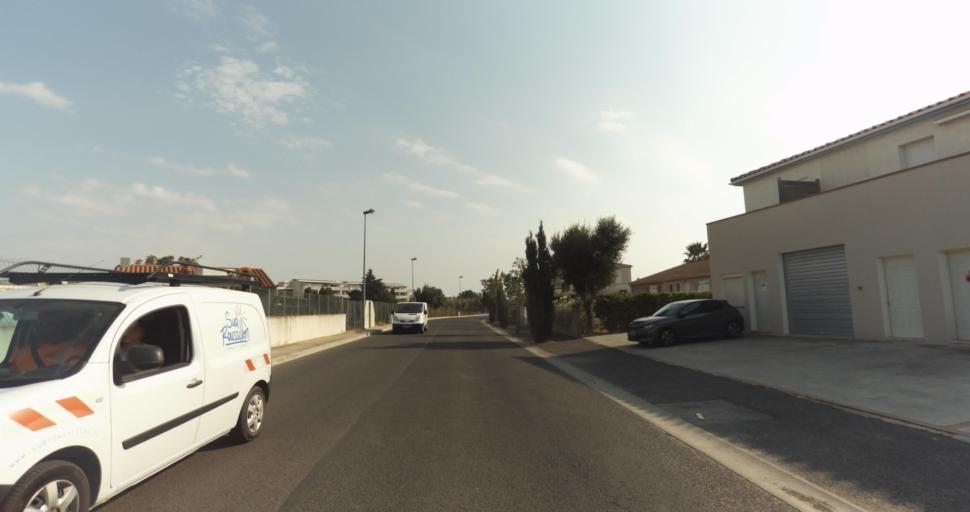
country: FR
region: Languedoc-Roussillon
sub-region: Departement des Pyrenees-Orientales
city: Latour-Bas-Elne
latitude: 42.6152
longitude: 2.9943
